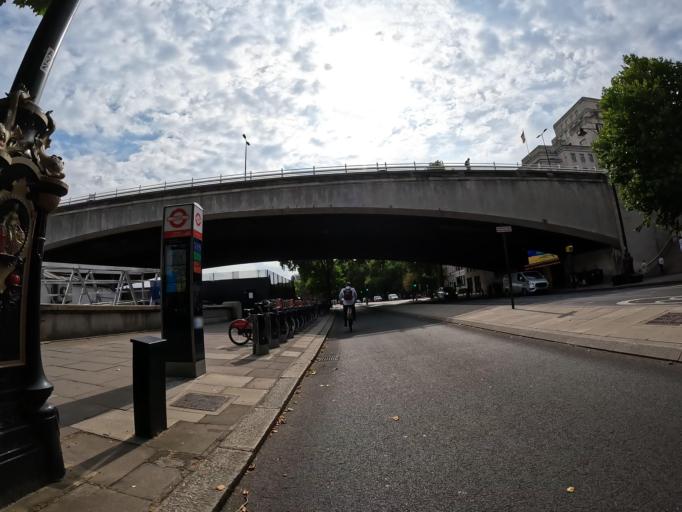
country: GB
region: England
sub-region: Greater London
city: City of London
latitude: 51.5011
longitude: -0.0678
